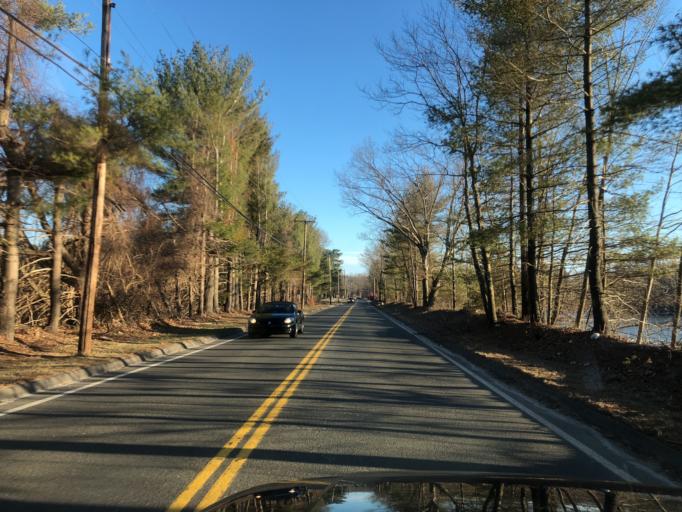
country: US
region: Connecticut
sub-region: Hartford County
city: Farmington
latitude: 41.7443
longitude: -72.8534
